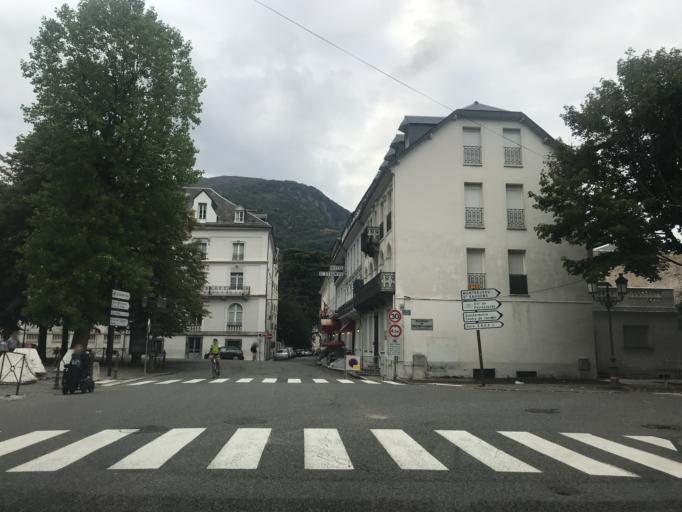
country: FR
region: Midi-Pyrenees
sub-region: Departement de la Haute-Garonne
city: Bagneres-de-Luchon
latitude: 42.7853
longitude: 0.5955
